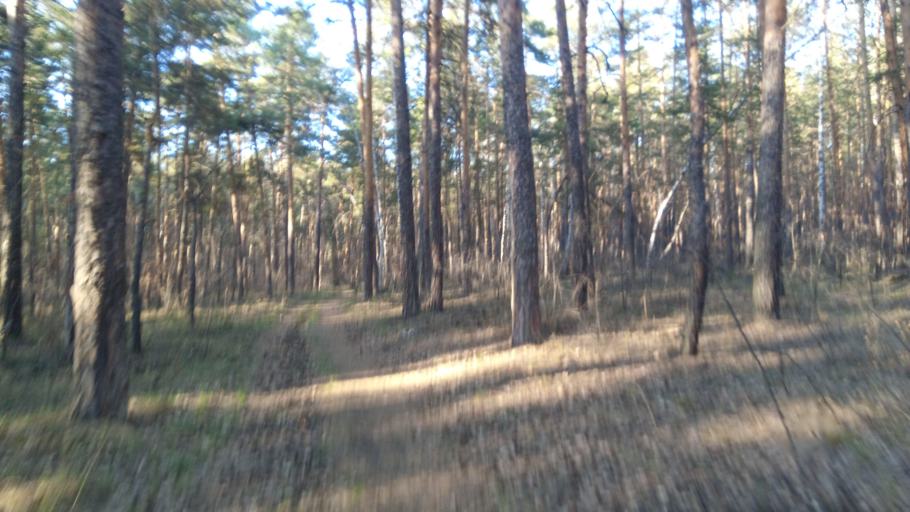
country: RU
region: Chelyabinsk
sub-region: Gorod Chelyabinsk
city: Chelyabinsk
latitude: 55.1351
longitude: 61.3291
